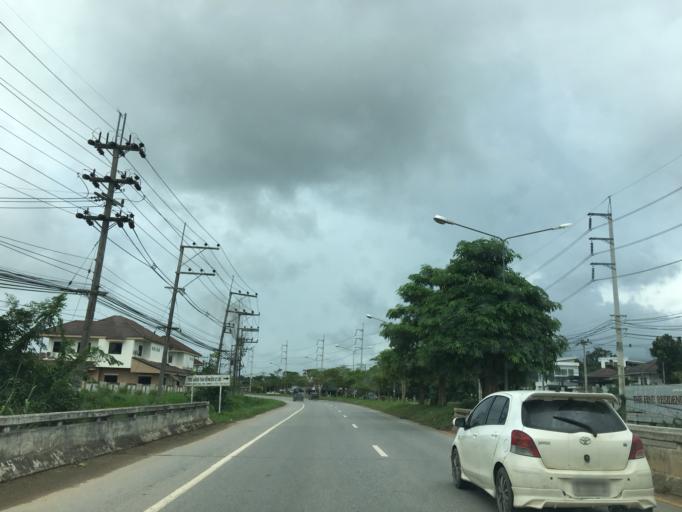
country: TH
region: Chiang Rai
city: Chiang Rai
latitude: 19.8543
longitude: 99.8474
